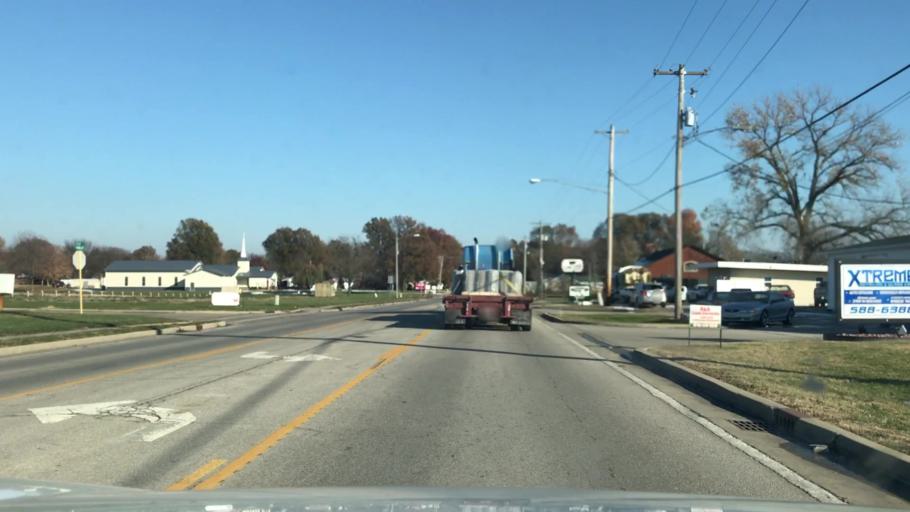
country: US
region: Illinois
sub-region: Clinton County
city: New Baden
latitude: 38.5351
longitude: -89.7091
